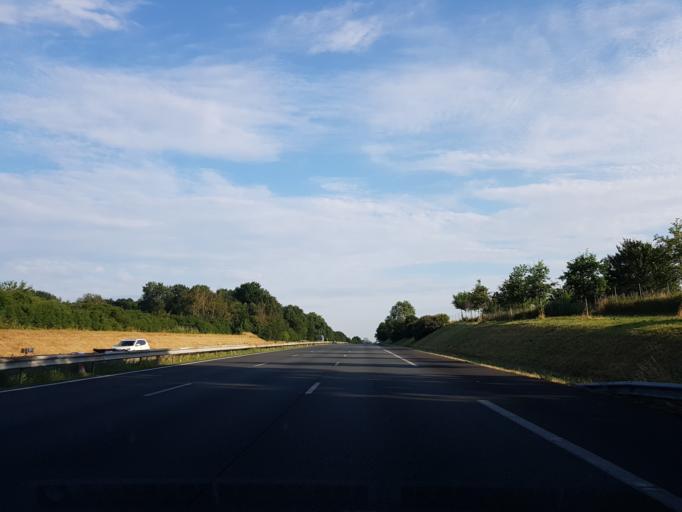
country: FR
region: Picardie
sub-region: Departement de l'Oise
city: Ressons-sur-Matz
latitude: 49.6141
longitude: 2.7552
